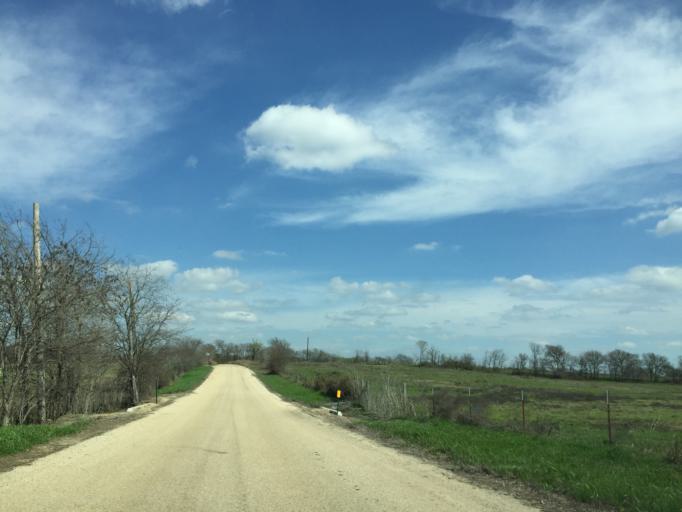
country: US
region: Texas
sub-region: Milam County
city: Thorndale
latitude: 30.5604
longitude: -97.1990
